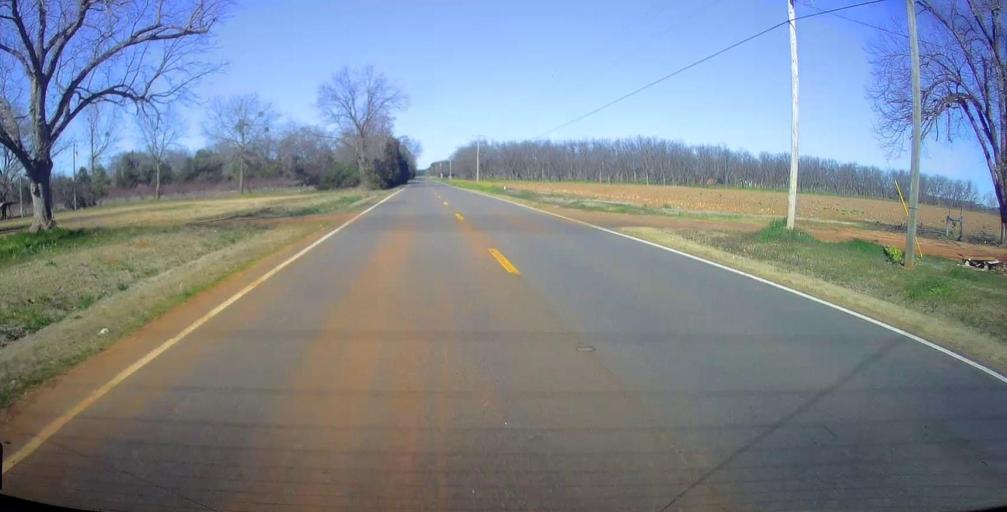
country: US
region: Georgia
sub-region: Macon County
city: Montezuma
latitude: 32.3357
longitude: -84.0208
